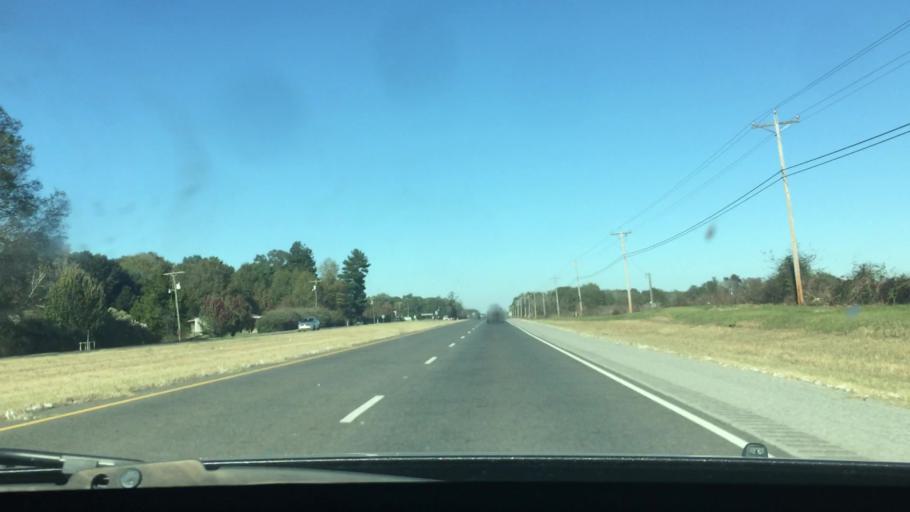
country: US
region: Louisiana
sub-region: Richland Parish
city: Rayville
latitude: 32.4020
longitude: -91.7685
